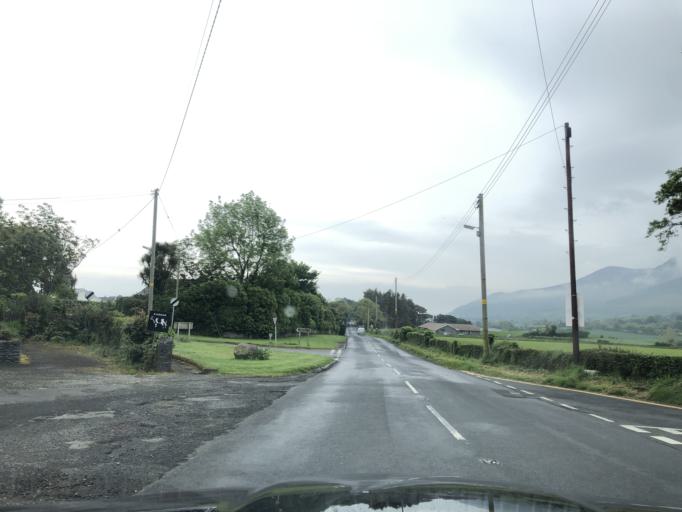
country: GB
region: Northern Ireland
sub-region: Down District
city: Newcastle
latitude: 54.2267
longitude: -5.9222
